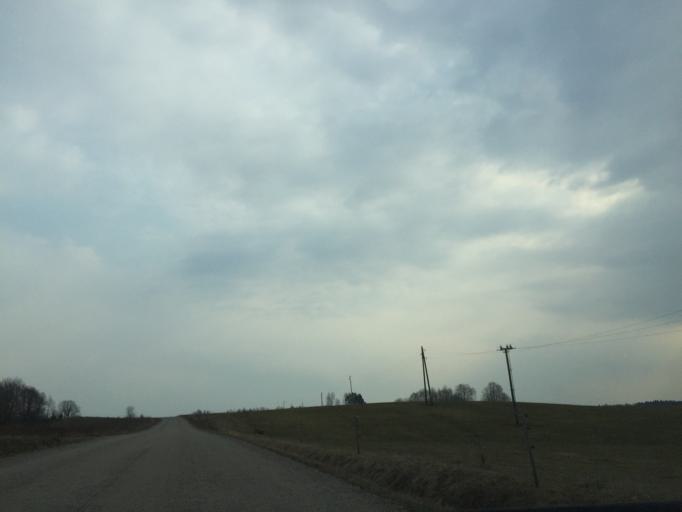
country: LV
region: Priekuli
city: Priekuli
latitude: 57.2426
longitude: 25.3738
